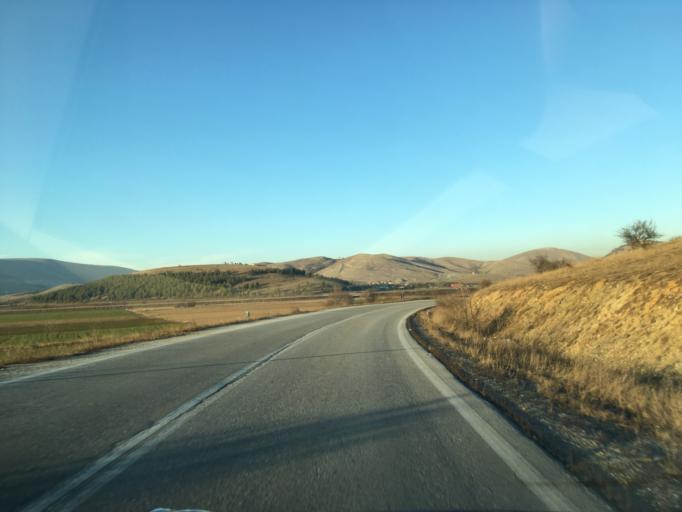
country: GR
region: West Macedonia
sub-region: Nomos Kozanis
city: Kozani
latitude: 40.3128
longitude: 21.7318
